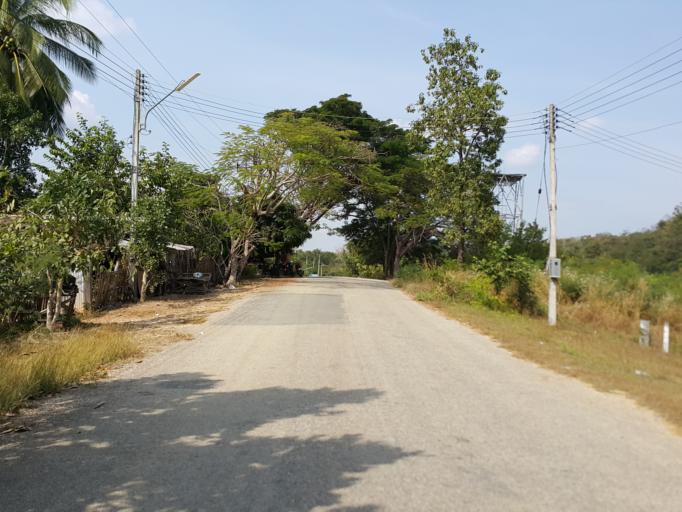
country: TH
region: Sukhothai
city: Thung Saliam
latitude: 17.3454
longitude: 99.4382
